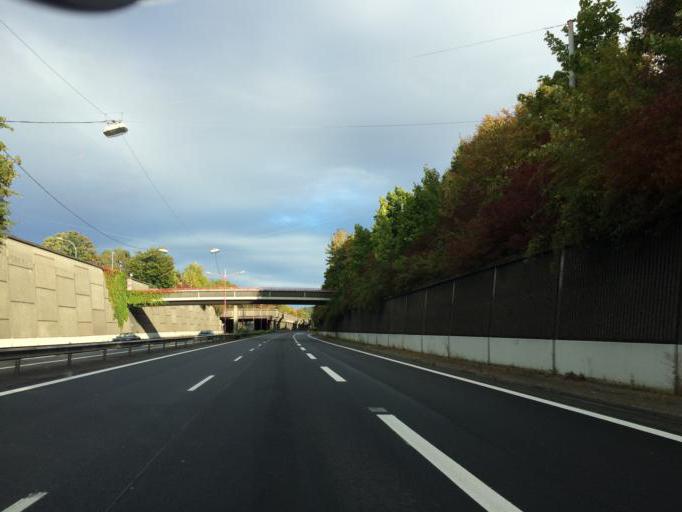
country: DE
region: North Rhine-Westphalia
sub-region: Regierungsbezirk Koln
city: Konigswinter
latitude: 50.7014
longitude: 7.1809
